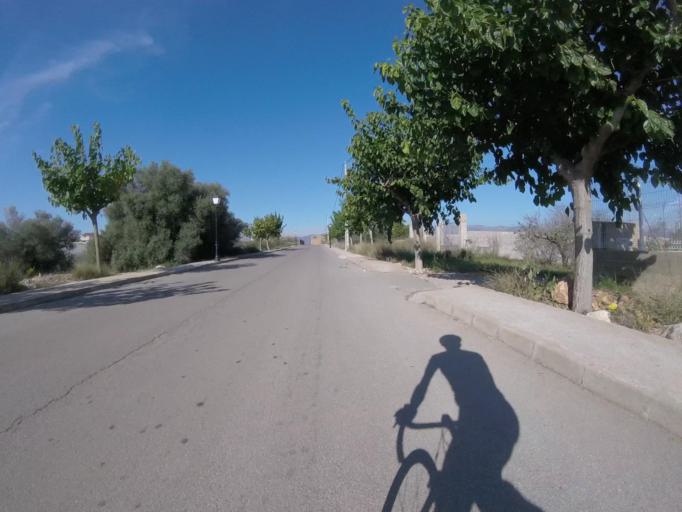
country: ES
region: Valencia
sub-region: Provincia de Castello
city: Benlloch
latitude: 40.2343
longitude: 0.0761
